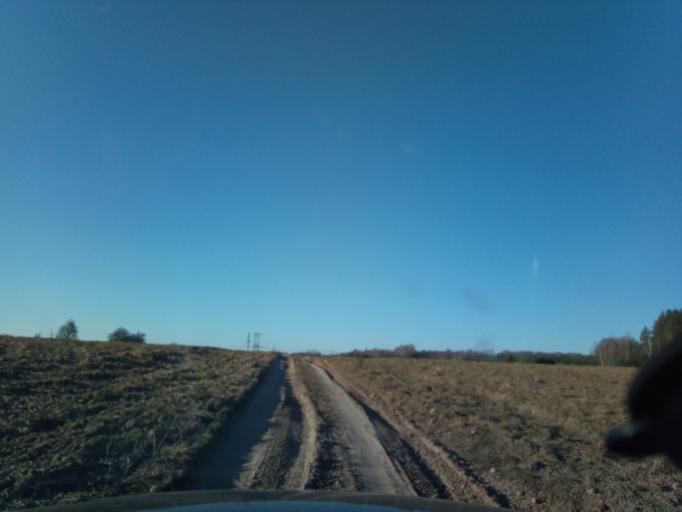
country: LT
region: Alytaus apskritis
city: Druskininkai
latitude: 53.9833
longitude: 23.9026
